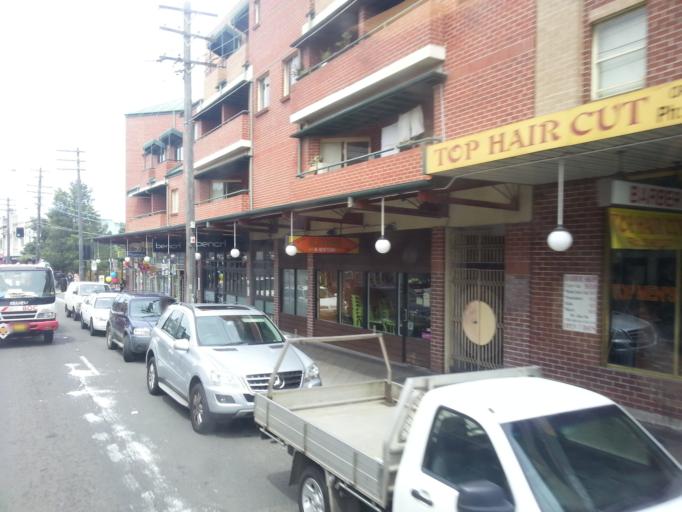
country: AU
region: New South Wales
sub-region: Marrickville
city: Newtown
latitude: -33.9026
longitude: 151.1792
